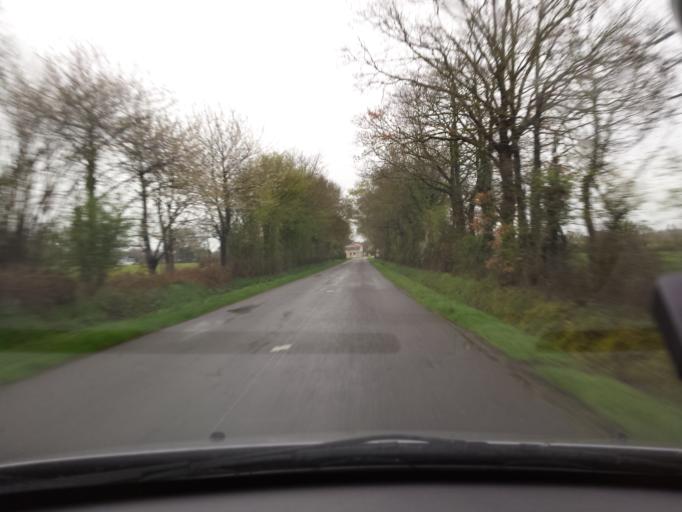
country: FR
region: Pays de la Loire
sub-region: Departement de la Vendee
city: Chauche
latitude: 46.7844
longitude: -1.3030
